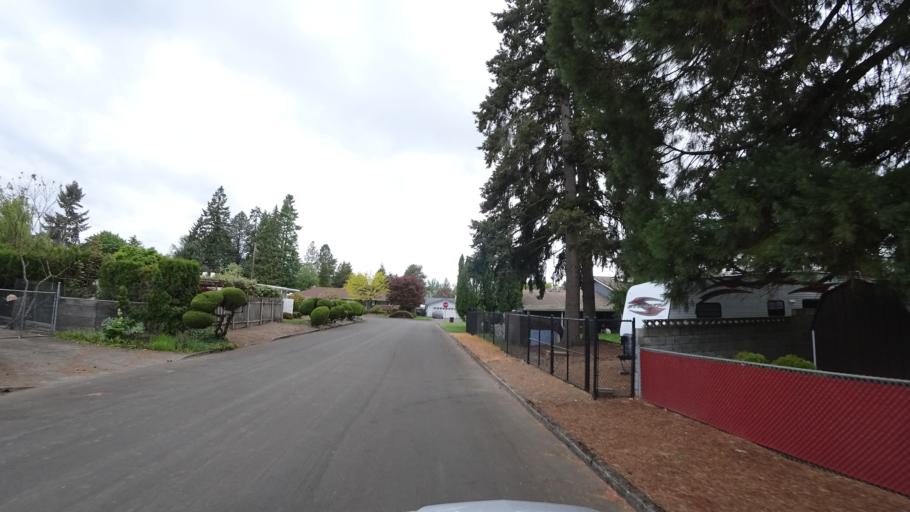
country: US
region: Oregon
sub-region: Washington County
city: Hillsboro
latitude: 45.5287
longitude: -122.9785
